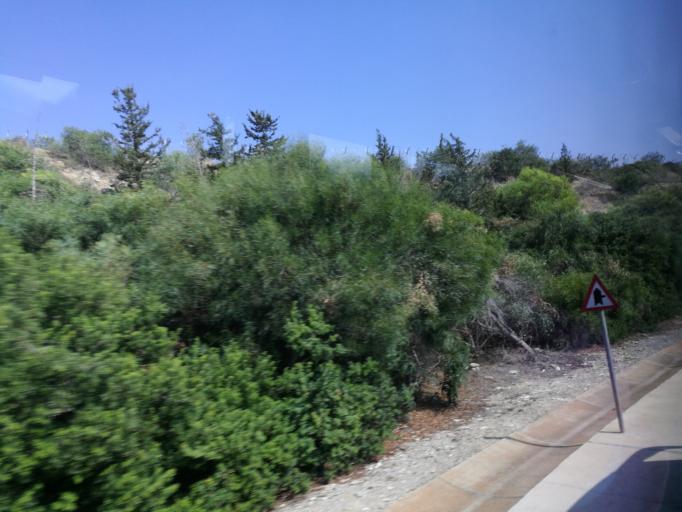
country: CY
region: Larnaka
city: Xylotymbou
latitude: 34.9901
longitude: 33.7233
